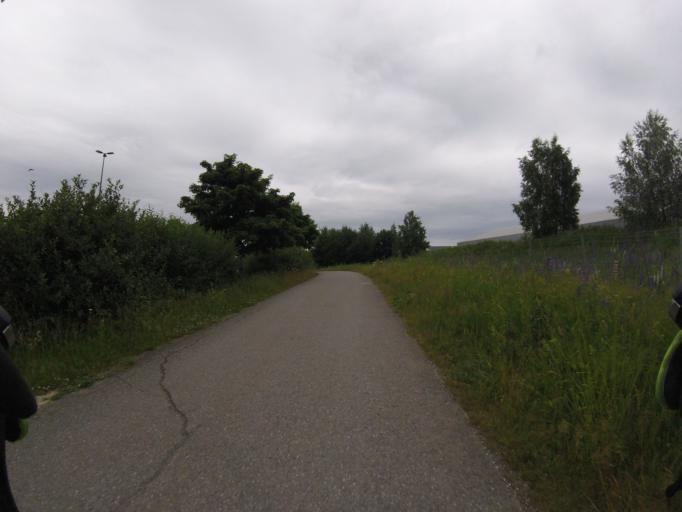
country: NO
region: Akershus
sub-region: Skedsmo
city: Lillestrom
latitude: 59.9696
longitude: 11.0493
